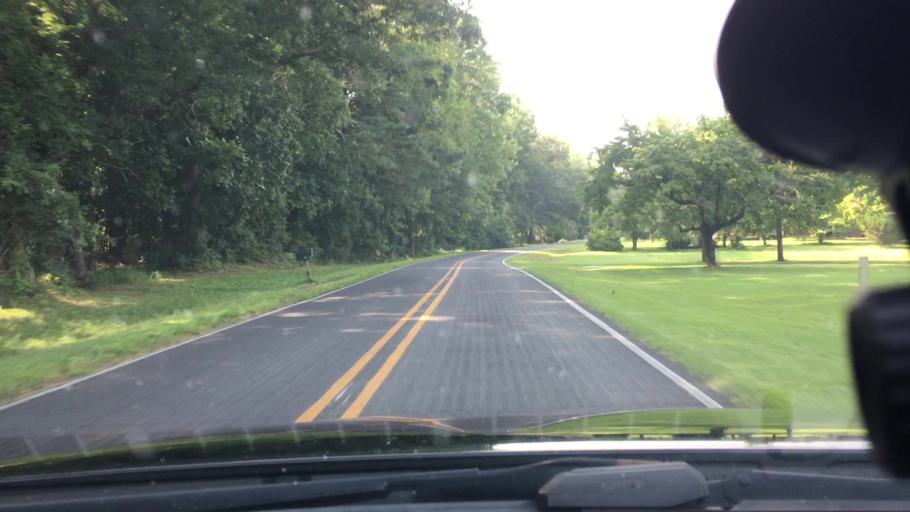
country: US
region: North Carolina
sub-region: Craven County
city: New Bern
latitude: 35.1793
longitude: -77.0555
